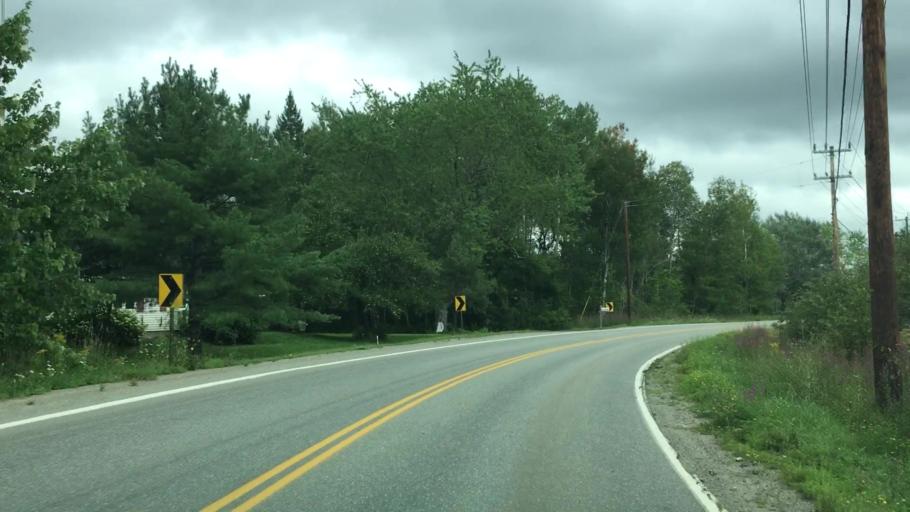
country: US
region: Maine
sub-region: Penobscot County
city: Brewer
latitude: 44.7675
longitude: -68.7567
